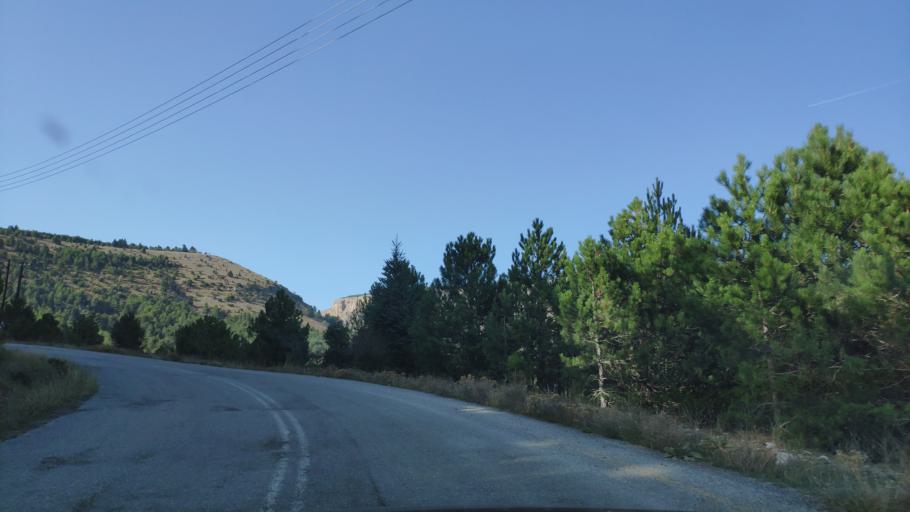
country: GR
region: West Greece
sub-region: Nomos Achaias
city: Aiyira
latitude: 38.0211
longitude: 22.4048
